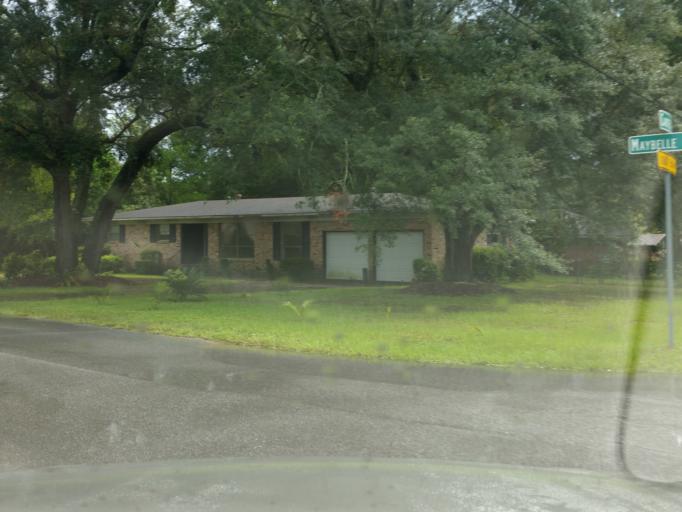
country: US
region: Florida
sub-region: Escambia County
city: Ferry Pass
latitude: 30.4992
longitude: -87.1954
